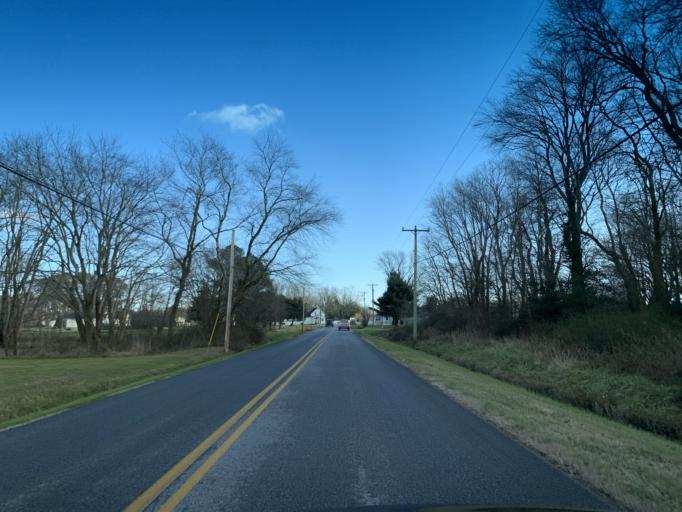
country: US
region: Maryland
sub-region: Worcester County
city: Ocean Pines
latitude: 38.4256
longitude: -75.1707
